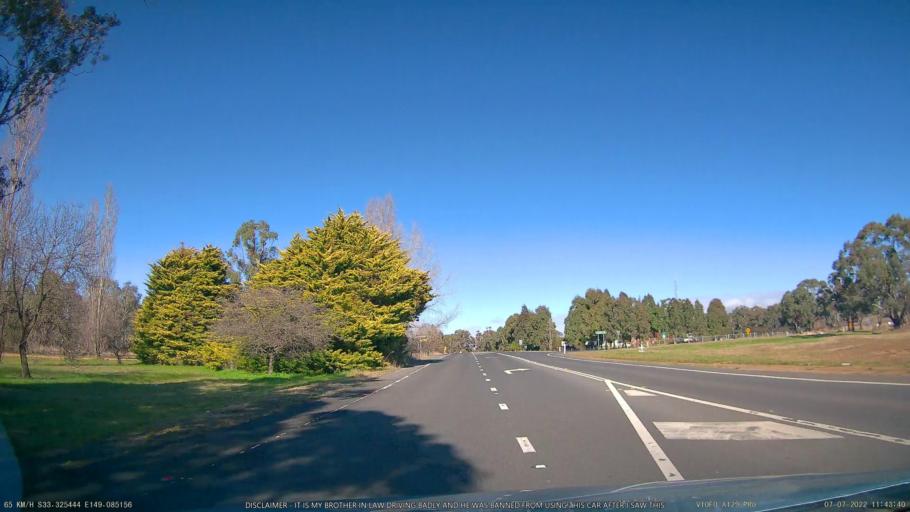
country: AU
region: New South Wales
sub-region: Orange Municipality
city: Orange
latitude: -33.3258
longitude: 149.0850
